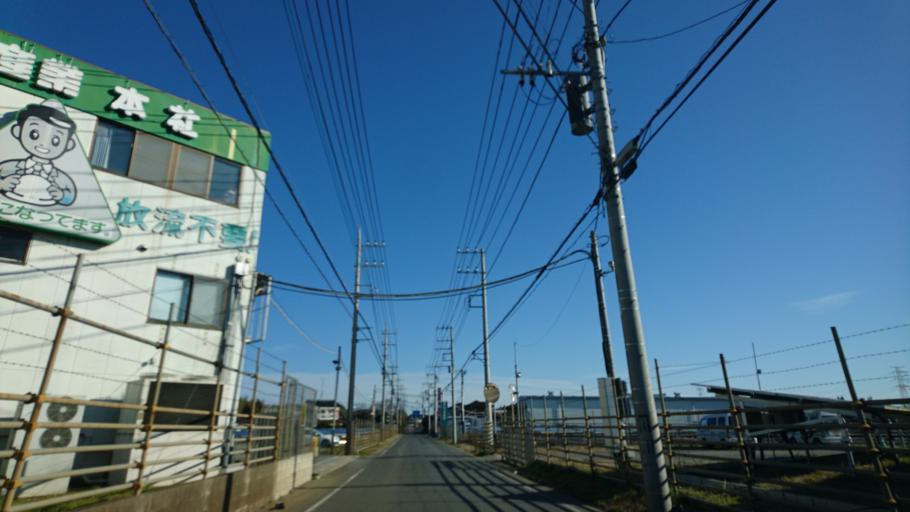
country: JP
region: Chiba
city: Togane
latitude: 35.5869
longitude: 140.3174
